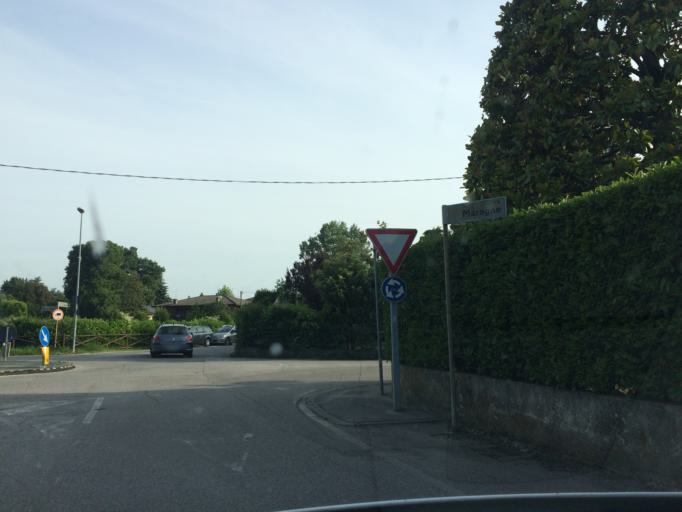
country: IT
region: Veneto
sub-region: Provincia di Padova
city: Cittadella
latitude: 45.6529
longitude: 11.7787
